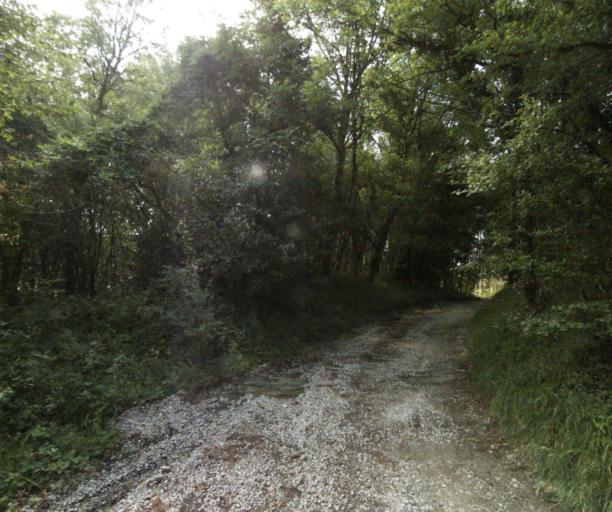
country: FR
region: Midi-Pyrenees
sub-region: Departement du Tarn
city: Dourgne
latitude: 43.4582
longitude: 2.1199
